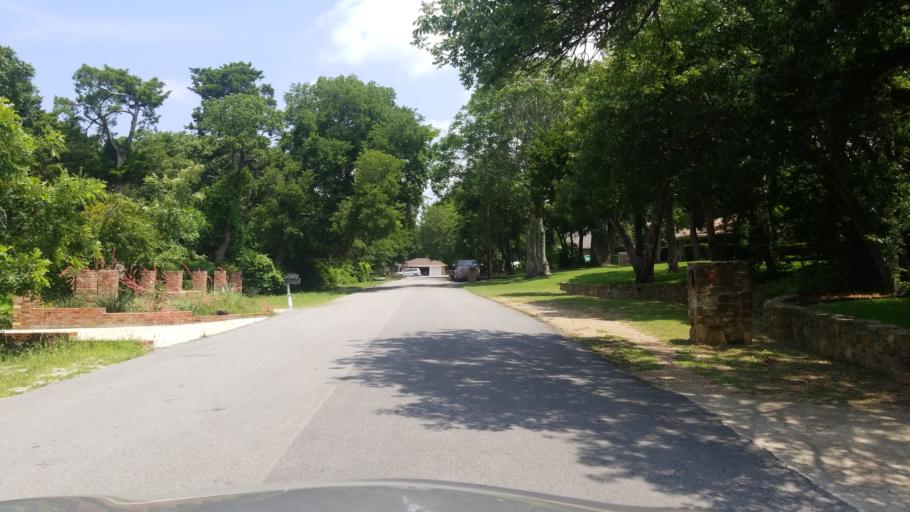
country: US
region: Texas
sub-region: Dallas County
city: Duncanville
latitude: 32.6788
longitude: -96.9215
